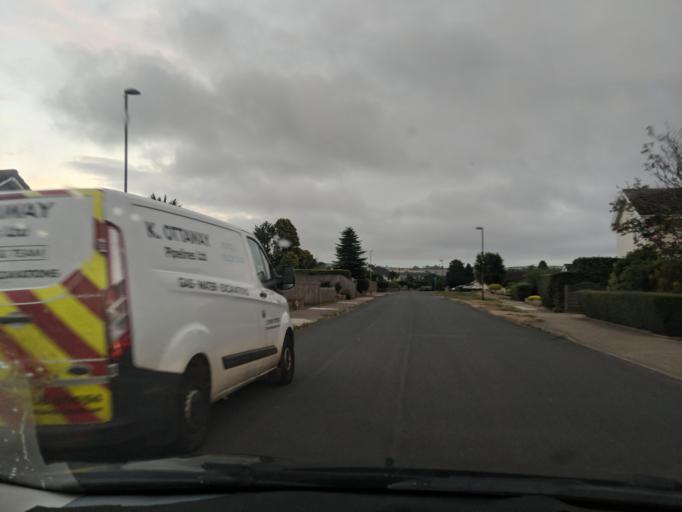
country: GB
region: England
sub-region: Borough of Torbay
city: Paignton
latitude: 50.4076
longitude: -3.5670
